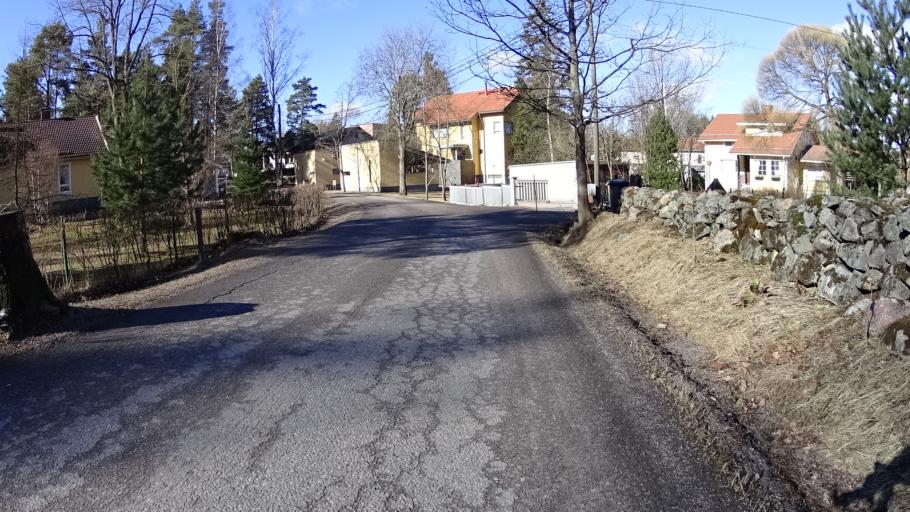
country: FI
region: Uusimaa
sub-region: Helsinki
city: Teekkarikylae
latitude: 60.2582
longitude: 24.8749
